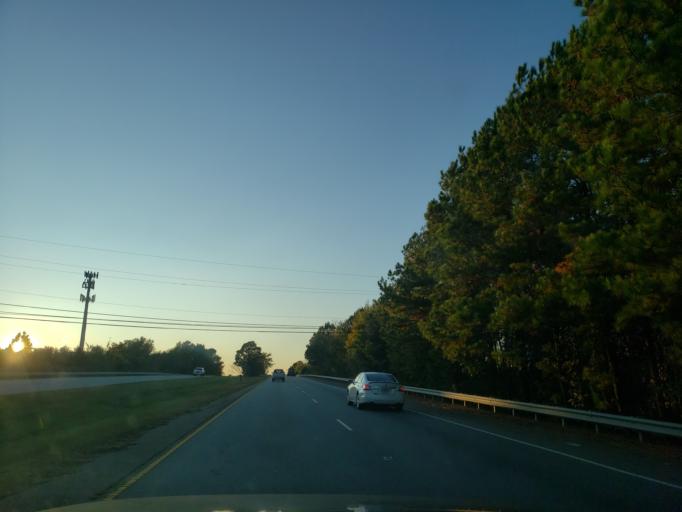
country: US
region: North Carolina
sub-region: Wake County
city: Apex
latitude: 35.7489
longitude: -78.8451
